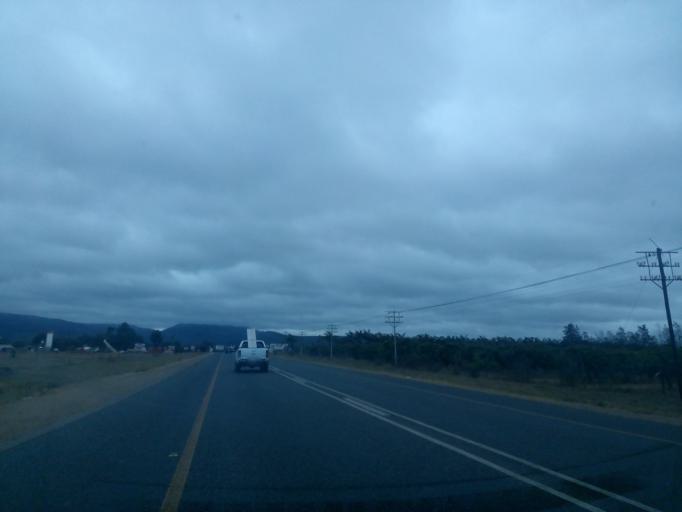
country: ZA
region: Limpopo
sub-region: Vhembe District Municipality
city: Louis Trichardt
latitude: -23.0749
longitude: 29.9098
